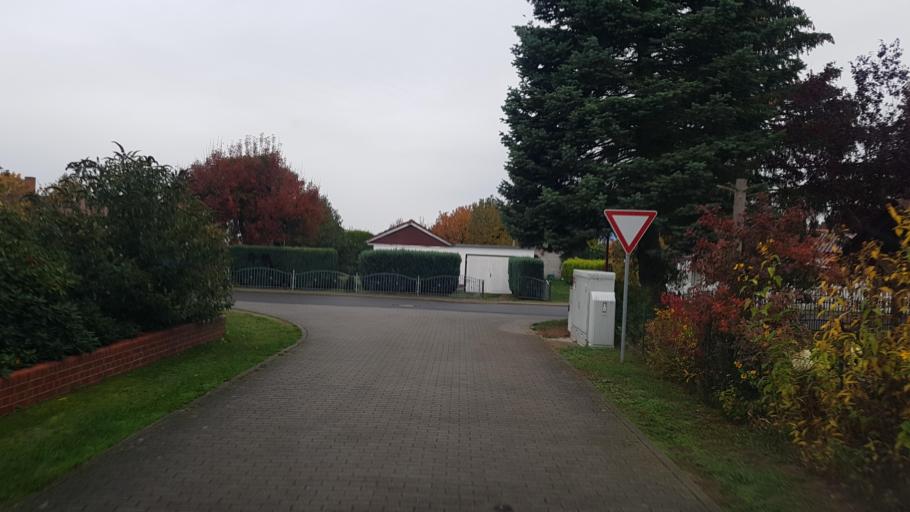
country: DE
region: Brandenburg
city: Schlieben
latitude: 51.7375
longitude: 13.3804
